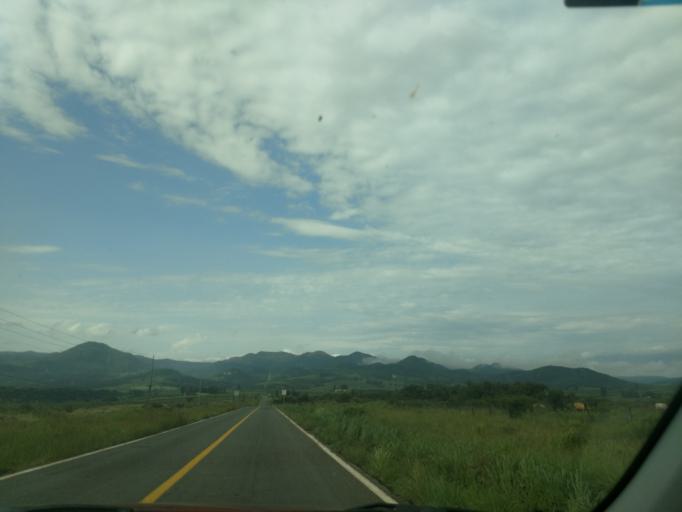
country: MX
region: Jalisco
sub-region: Atengo
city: Soyatlan del Oro
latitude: 20.5348
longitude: -104.3150
